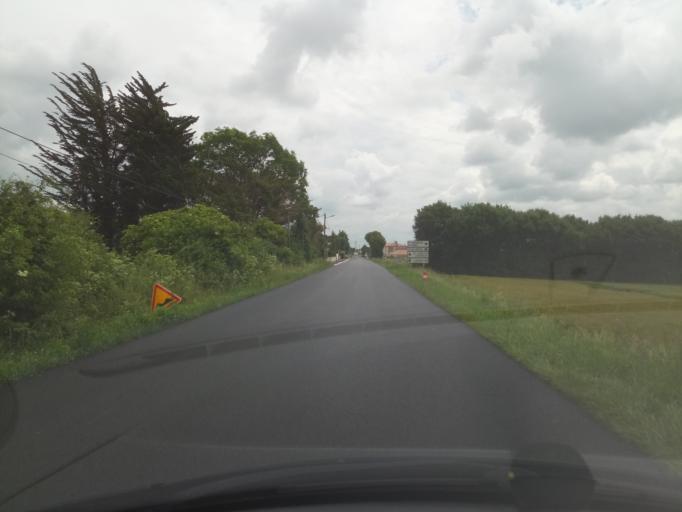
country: FR
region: Poitou-Charentes
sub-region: Departement de la Charente-Maritime
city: Saint-Jean-de-Liversay
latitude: 46.2686
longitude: -0.8850
